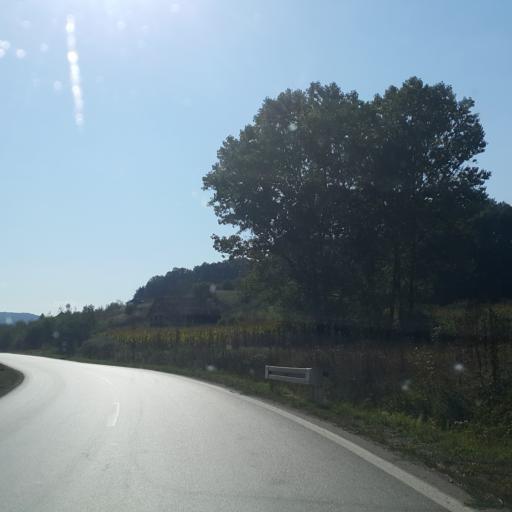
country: RS
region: Central Serbia
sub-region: Nisavski Okrug
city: Svrljig
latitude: 43.4094
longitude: 22.0987
